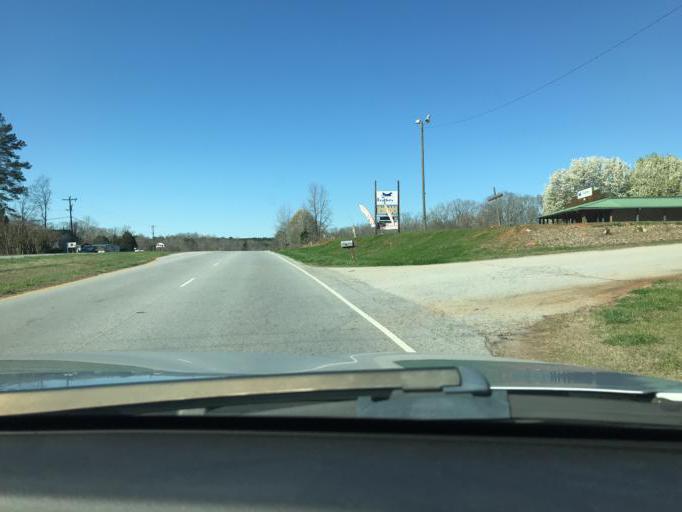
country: US
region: South Carolina
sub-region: Laurens County
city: Clinton
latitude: 34.4720
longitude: -81.9167
